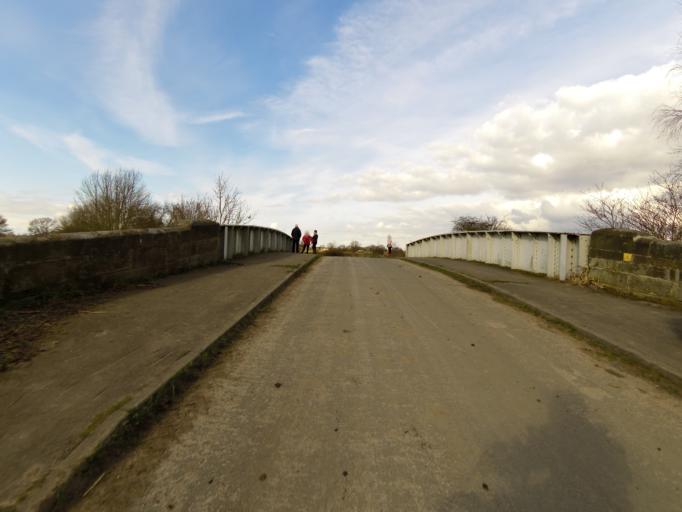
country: GB
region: England
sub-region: East Riding of Yorkshire
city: Pollington
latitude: 53.6630
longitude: -1.0570
